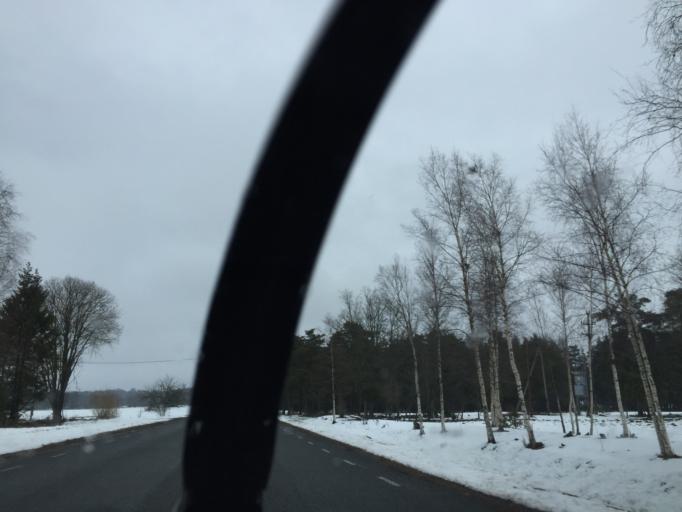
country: EE
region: Saare
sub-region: Kuressaare linn
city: Kuressaare
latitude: 58.3483
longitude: 22.0321
